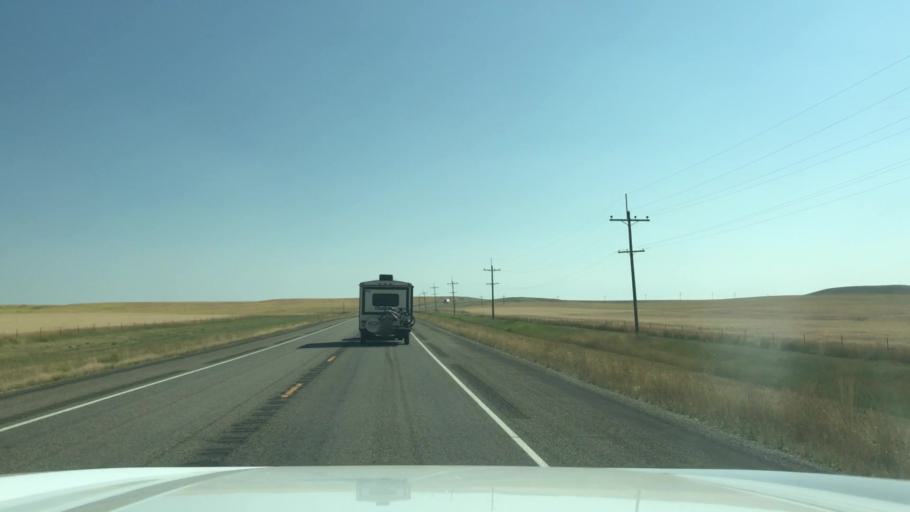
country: US
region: Montana
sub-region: Wheatland County
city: Harlowton
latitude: 46.4795
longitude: -109.7661
